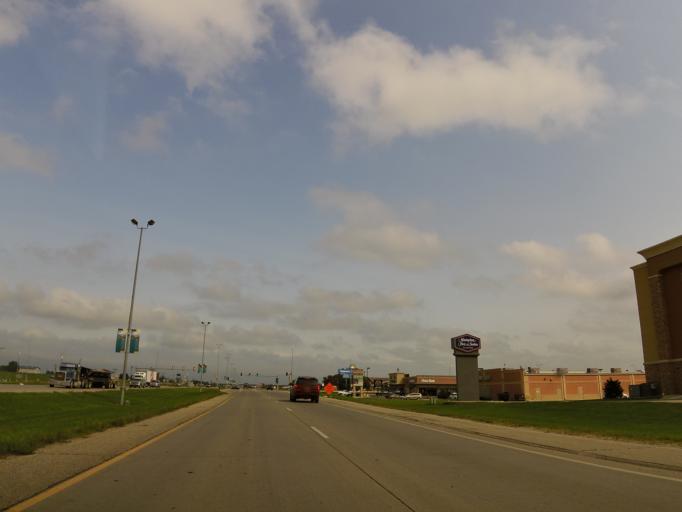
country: US
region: South Dakota
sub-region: Codington County
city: Watertown
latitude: 44.8900
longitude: -97.0708
